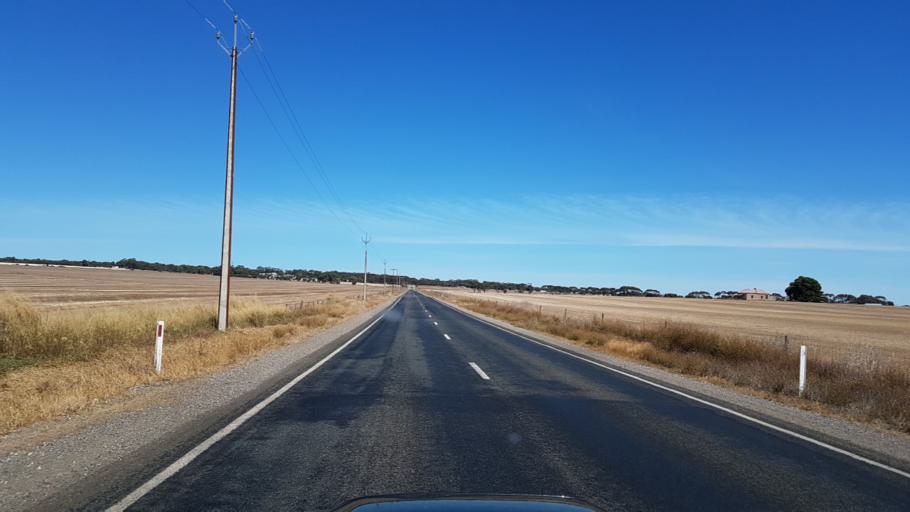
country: AU
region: South Australia
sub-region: Yorke Peninsula
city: Maitland
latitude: -34.3533
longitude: 137.6634
